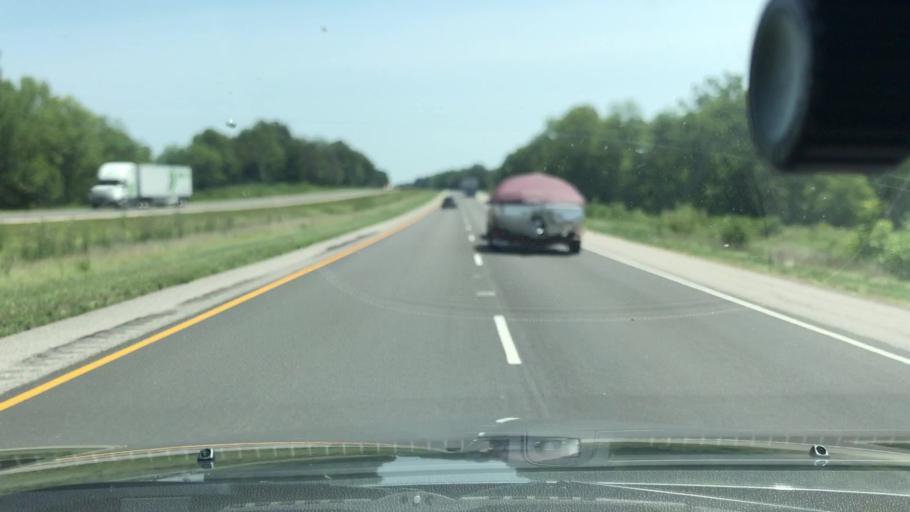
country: US
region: Illinois
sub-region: Clinton County
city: Wamac
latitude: 38.3885
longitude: -89.1643
